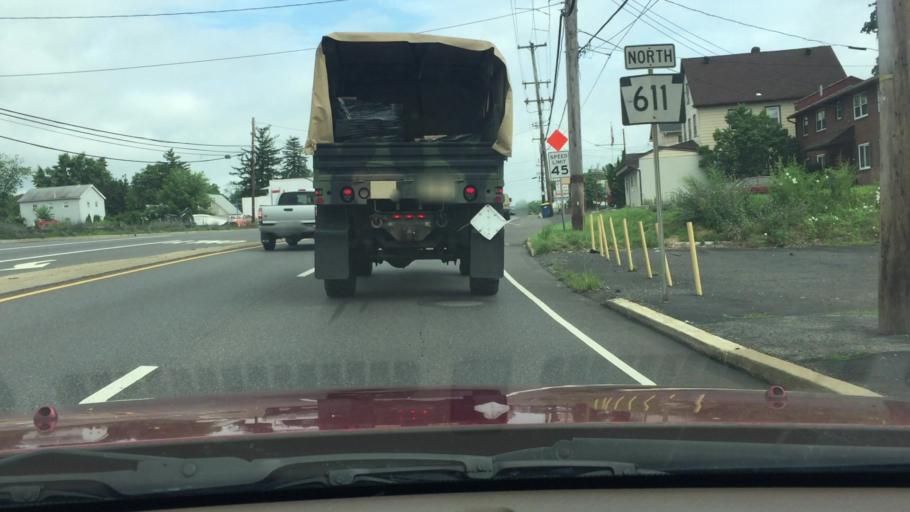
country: US
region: Pennsylvania
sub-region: Montgomery County
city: Horsham
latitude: 40.1719
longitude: -75.1279
